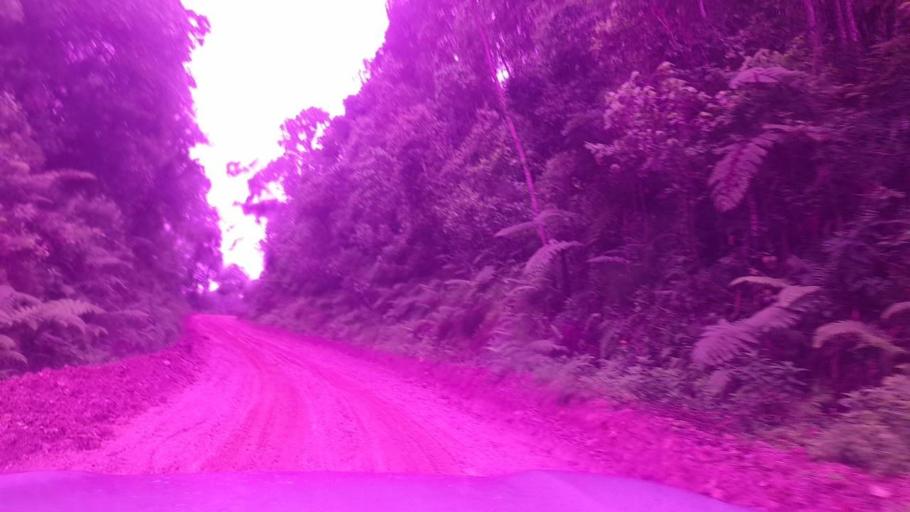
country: ET
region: Southern Nations, Nationalities, and People's Region
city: Bonga
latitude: 7.5056
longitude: 36.1035
